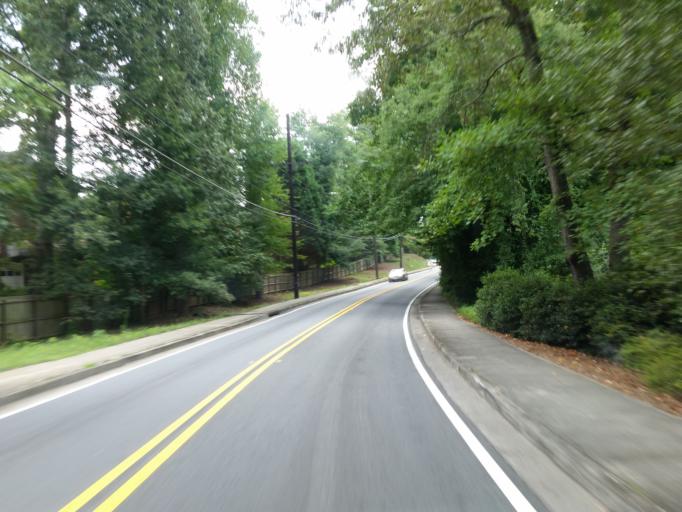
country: US
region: Georgia
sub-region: Cobb County
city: Vinings
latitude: 33.9372
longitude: -84.4579
